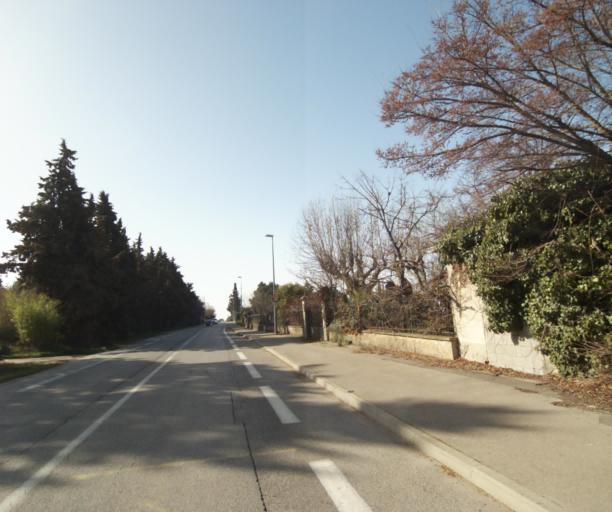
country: FR
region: Provence-Alpes-Cote d'Azur
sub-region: Departement des Bouches-du-Rhone
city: Aix-en-Provence
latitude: 43.5507
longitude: 5.4569
